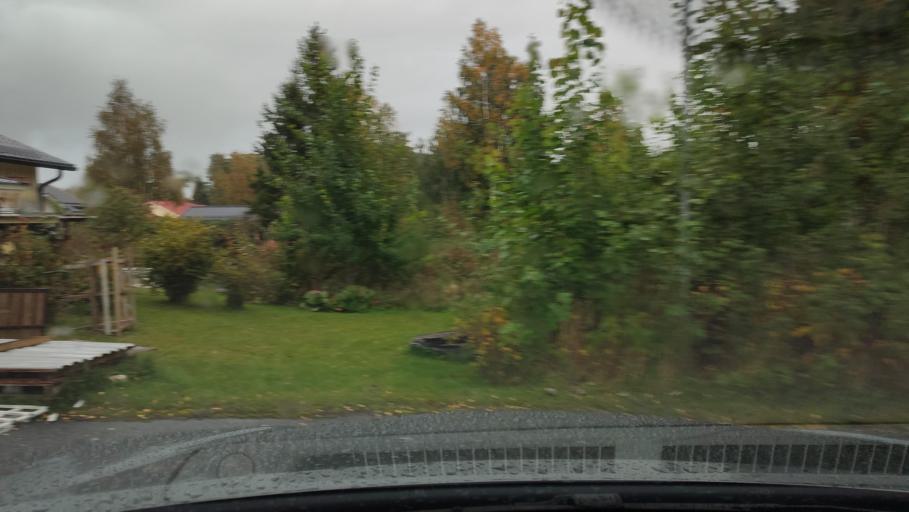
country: FI
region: Ostrobothnia
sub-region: Sydosterbotten
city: Kristinestad
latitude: 62.2786
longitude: 21.3515
